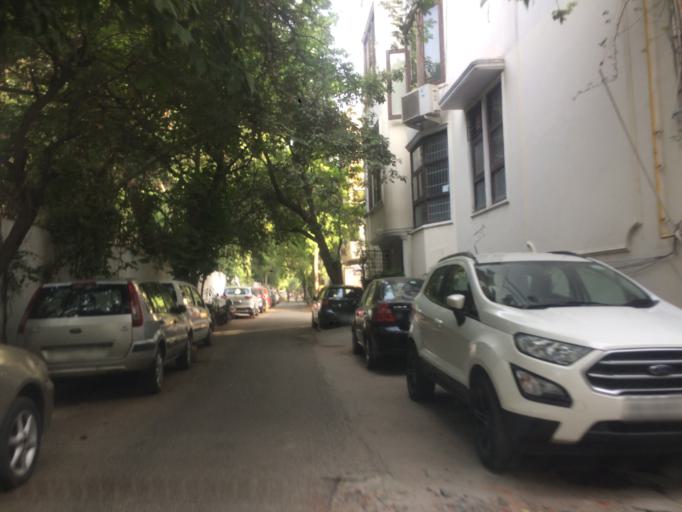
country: IN
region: NCT
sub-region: New Delhi
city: New Delhi
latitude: 28.5469
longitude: 77.2331
